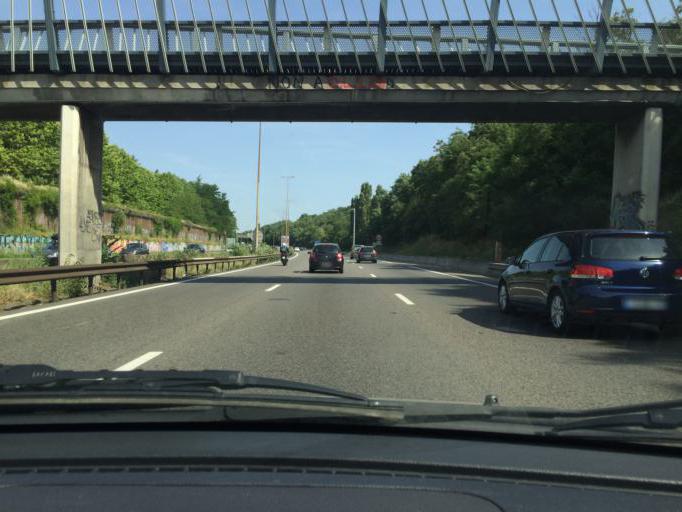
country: FR
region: Rhone-Alpes
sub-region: Departement du Rhone
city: Ecully
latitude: 45.7906
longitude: 4.7832
